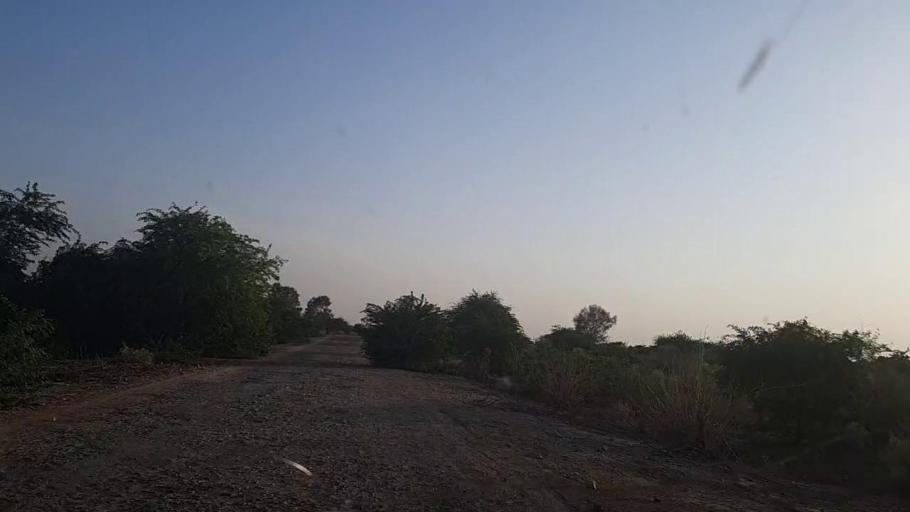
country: PK
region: Sindh
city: Khanpur
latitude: 27.6481
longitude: 69.4622
